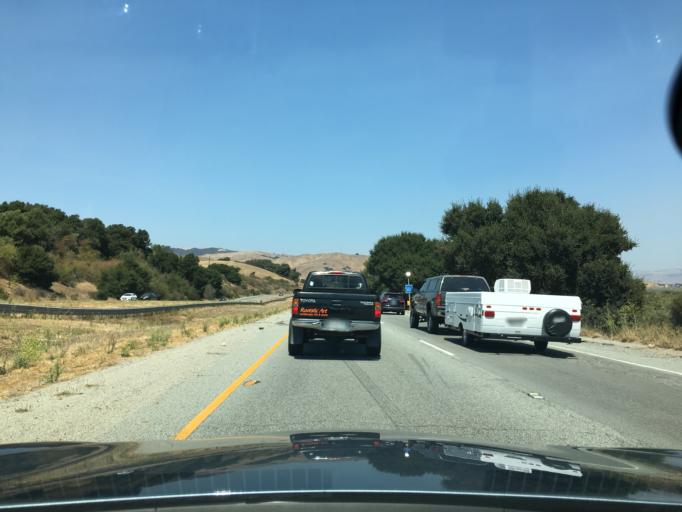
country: US
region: California
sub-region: Santa Clara County
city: Gilroy
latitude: 36.9307
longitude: -121.5488
